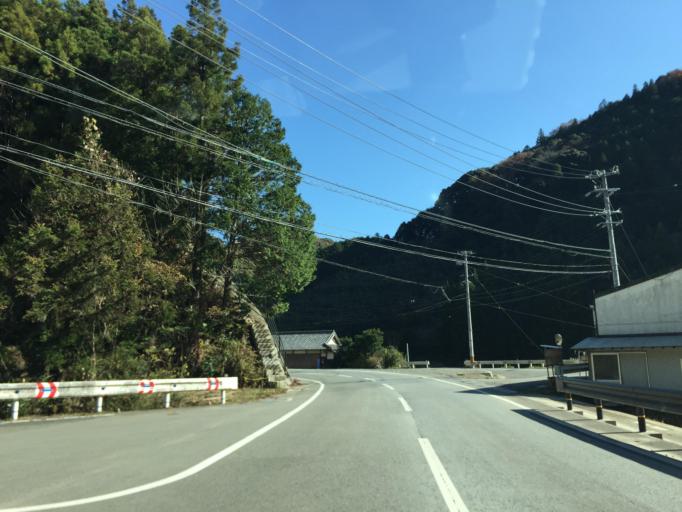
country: JP
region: Wakayama
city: Iwade
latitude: 34.1357
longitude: 135.3970
